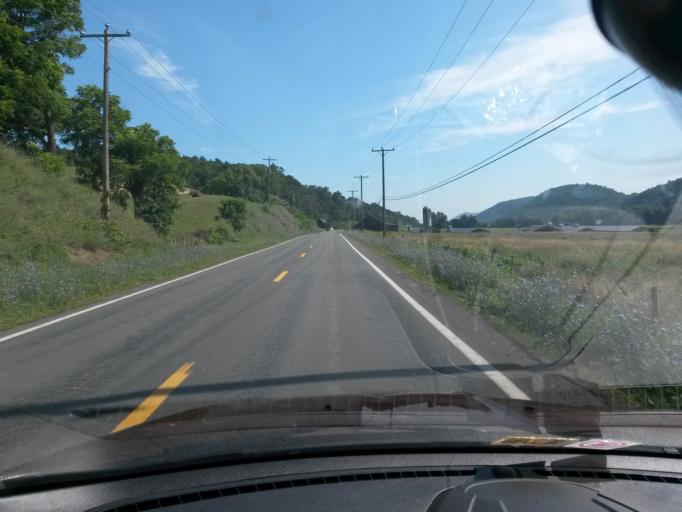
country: US
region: Virginia
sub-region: Shenandoah County
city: Basye
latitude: 38.9908
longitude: -78.7812
